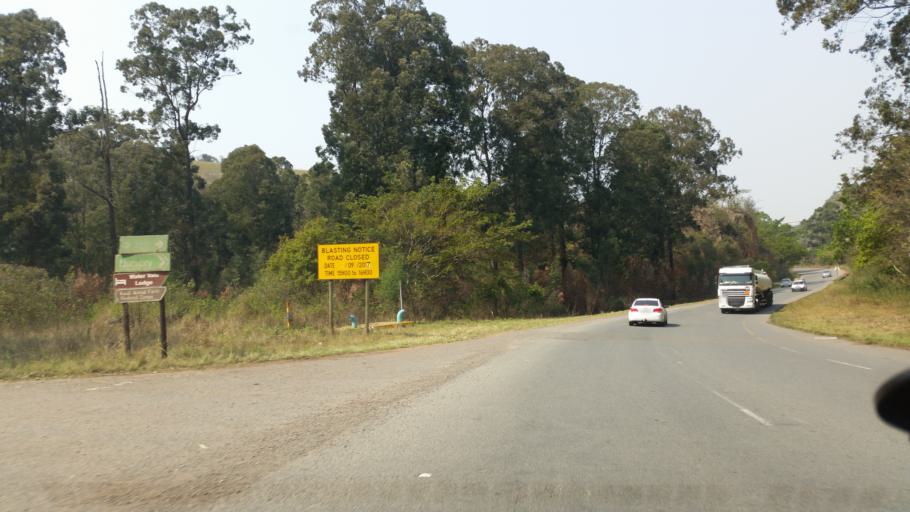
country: ZA
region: KwaZulu-Natal
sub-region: eThekwini Metropolitan Municipality
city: Mpumalanga
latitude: -29.7436
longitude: 30.6642
